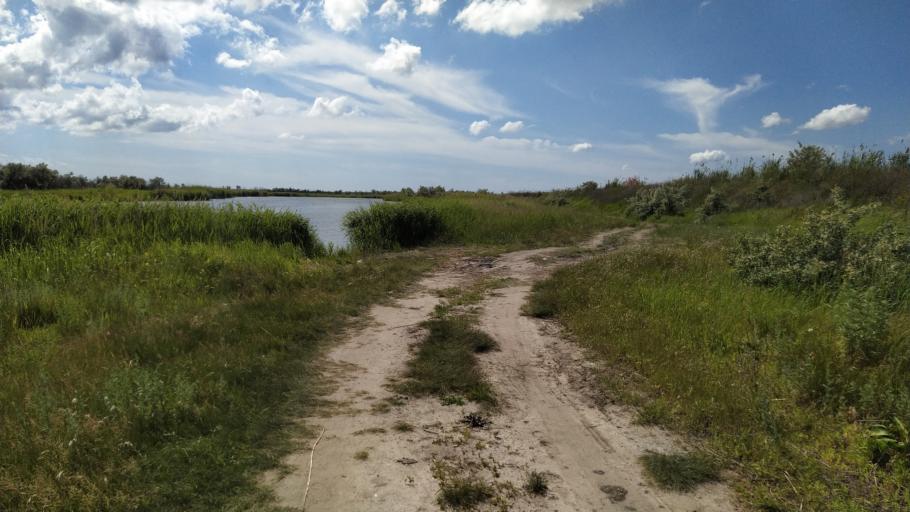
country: RU
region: Rostov
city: Bataysk
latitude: 47.1352
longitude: 39.6752
